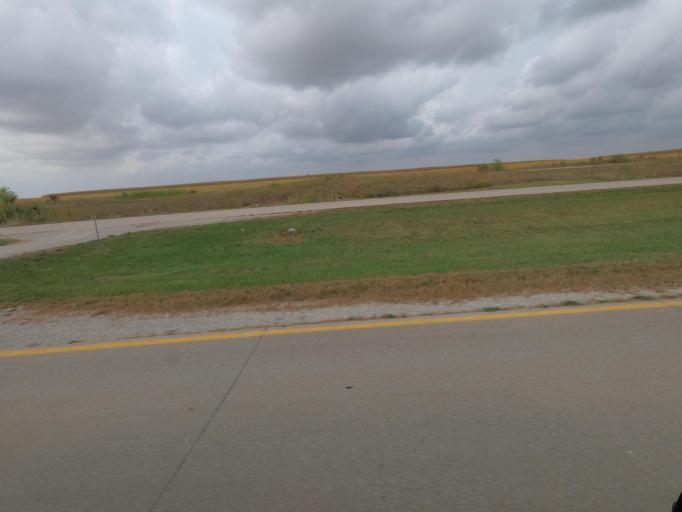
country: US
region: Iowa
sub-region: Wapello County
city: Ottumwa
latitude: 41.0039
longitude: -92.2911
